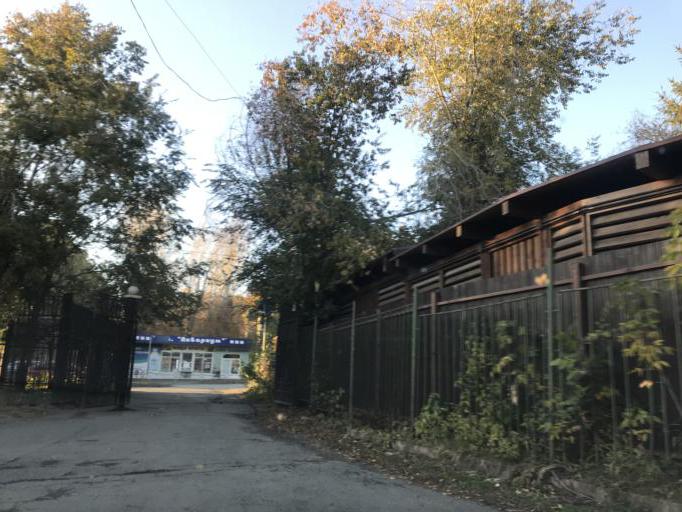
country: RU
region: Chelyabinsk
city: Dolgoderevenskoye
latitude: 55.2621
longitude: 61.3859
